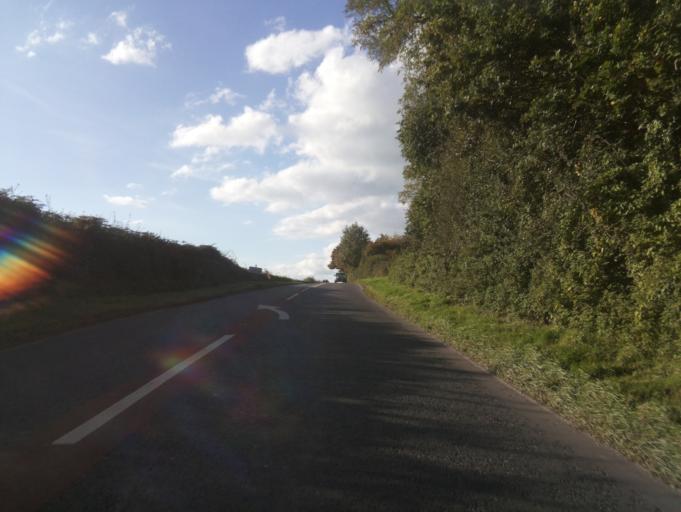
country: GB
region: England
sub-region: Herefordshire
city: Moccas
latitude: 52.0990
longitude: -2.9299
